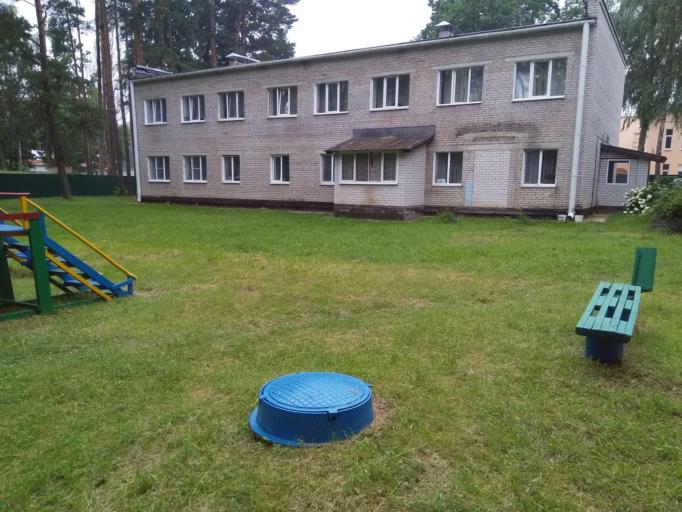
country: BY
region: Mogilev
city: Myazhysyatki
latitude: 53.8565
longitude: 30.1607
